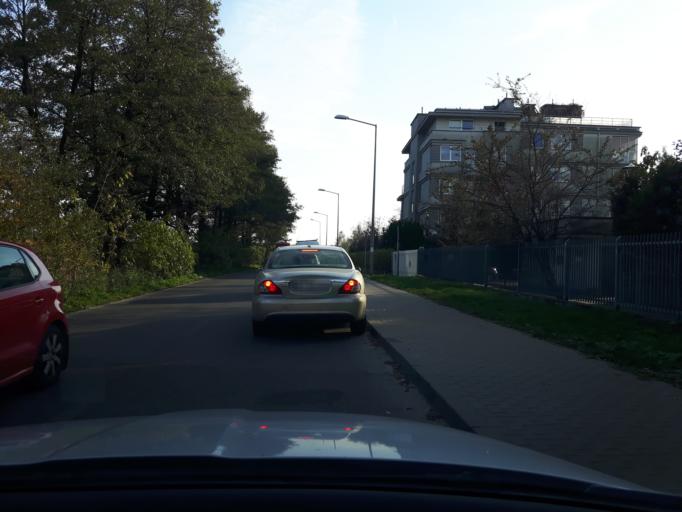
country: PL
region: Masovian Voivodeship
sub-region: Warszawa
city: Targowek
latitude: 52.3110
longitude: 21.0727
